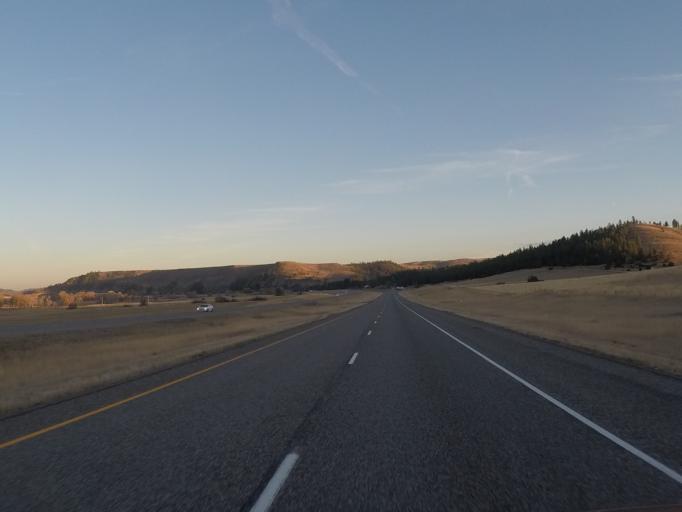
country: US
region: Montana
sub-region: Sweet Grass County
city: Big Timber
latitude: 45.7410
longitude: -109.7658
